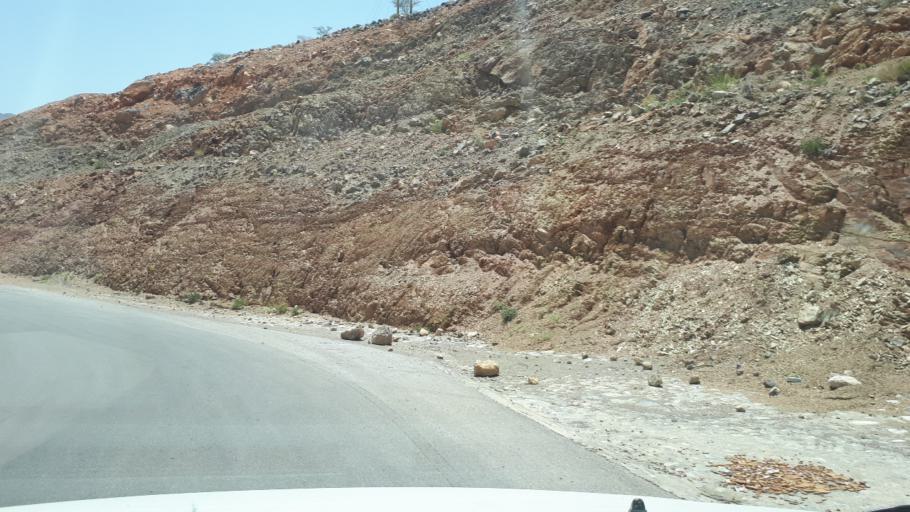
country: OM
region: Muhafazat ad Dakhiliyah
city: Bahla'
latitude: 23.1982
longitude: 57.1382
